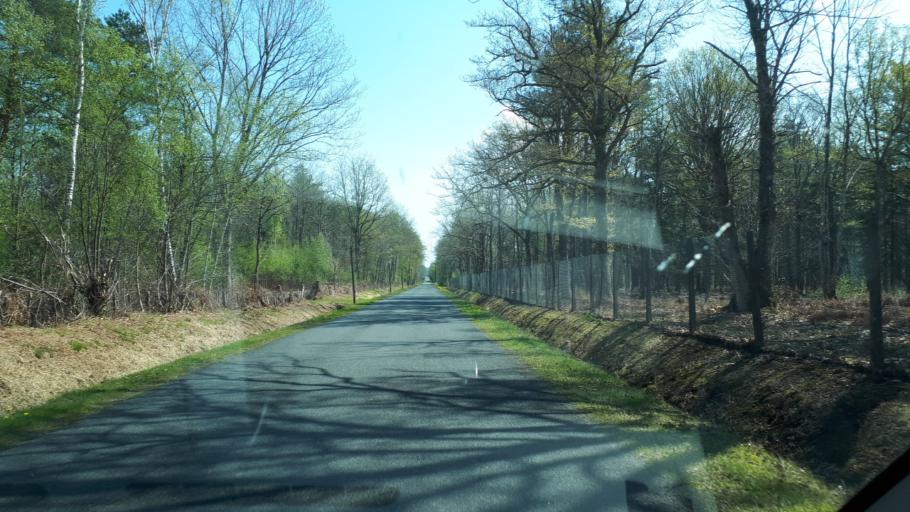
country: FR
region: Centre
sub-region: Departement du Cher
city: Neuvy-sur-Barangeon
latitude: 47.3175
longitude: 2.2311
